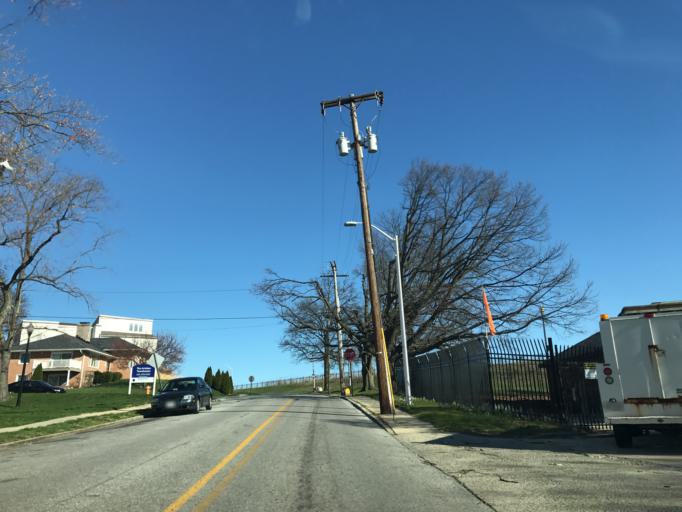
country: US
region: Maryland
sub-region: Baltimore County
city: Lochearn
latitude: 39.3181
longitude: -76.6690
